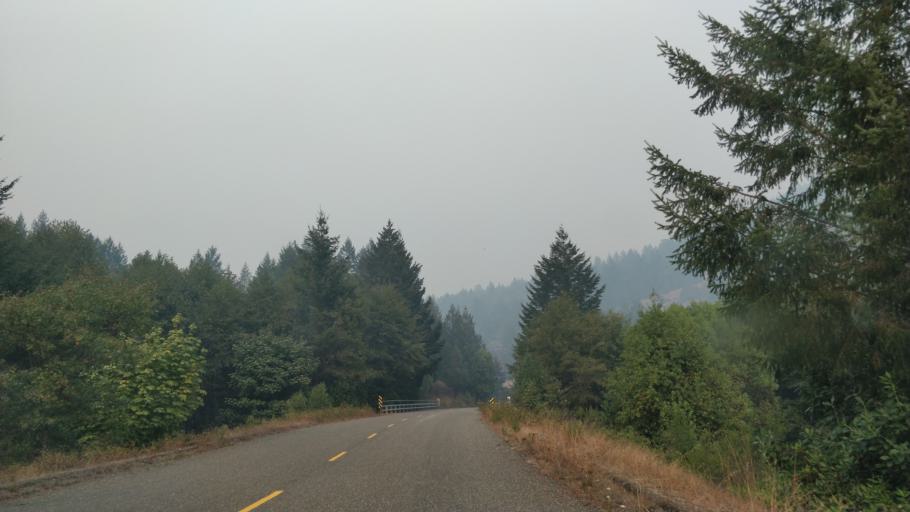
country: US
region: California
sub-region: Humboldt County
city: Rio Dell
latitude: 40.3326
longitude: -124.0279
